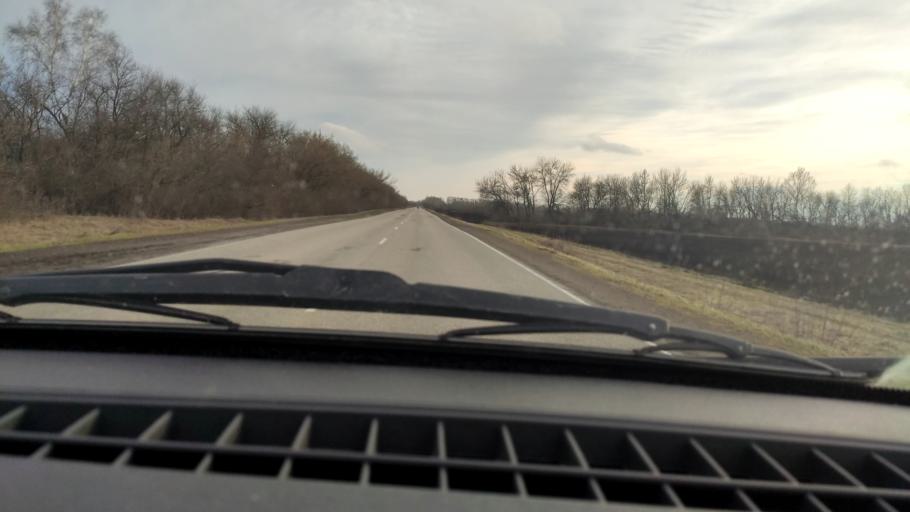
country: RU
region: Bashkortostan
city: Chishmy
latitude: 54.4652
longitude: 55.2587
